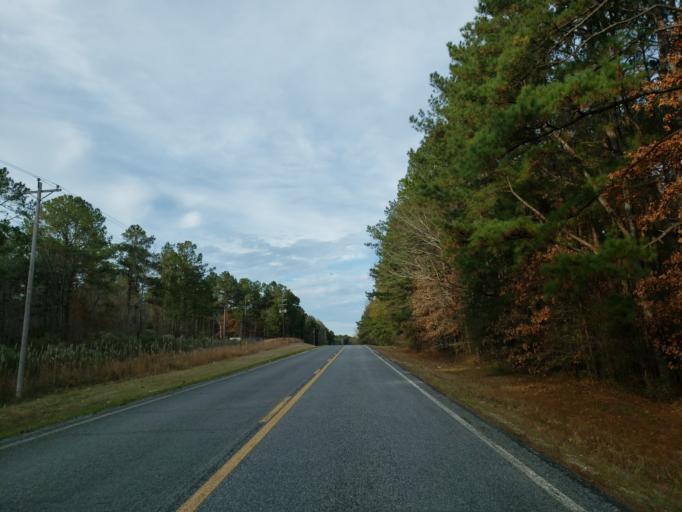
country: US
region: Mississippi
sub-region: Wayne County
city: Waynesboro
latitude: 31.8353
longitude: -88.6892
